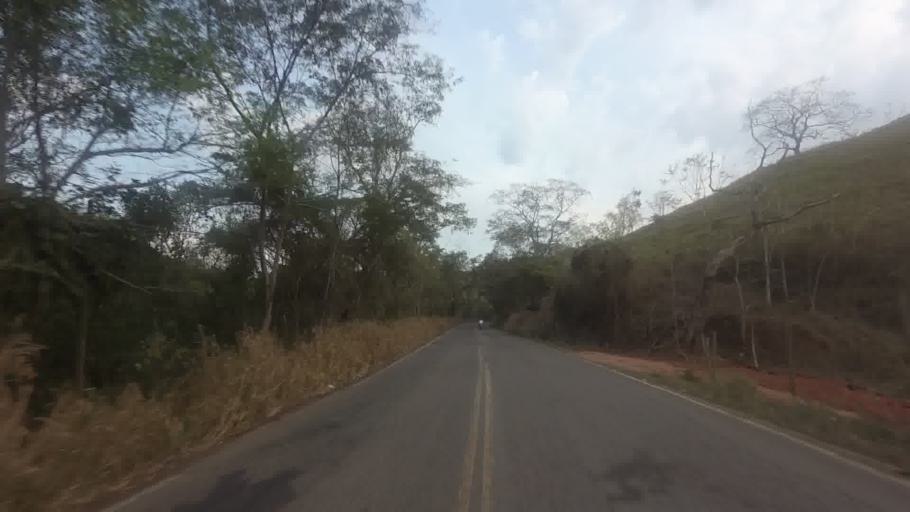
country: BR
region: Rio de Janeiro
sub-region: Santo Antonio De Padua
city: Santo Antonio de Padua
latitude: -21.5273
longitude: -42.1091
